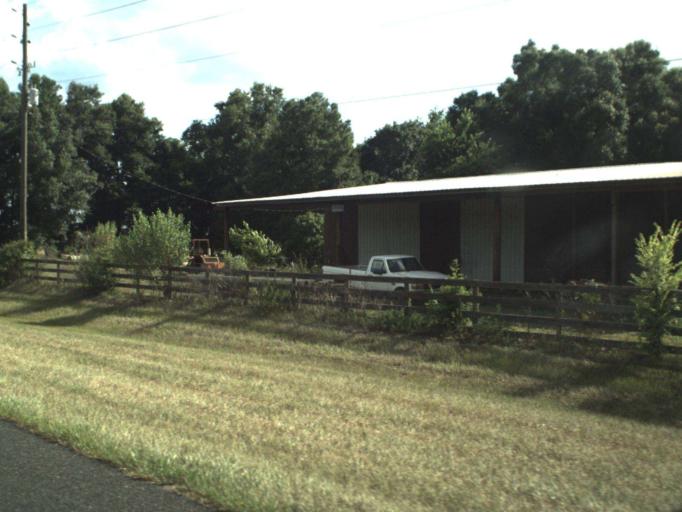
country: US
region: Florida
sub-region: Sumter County
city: The Villages
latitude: 28.9490
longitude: -82.0389
